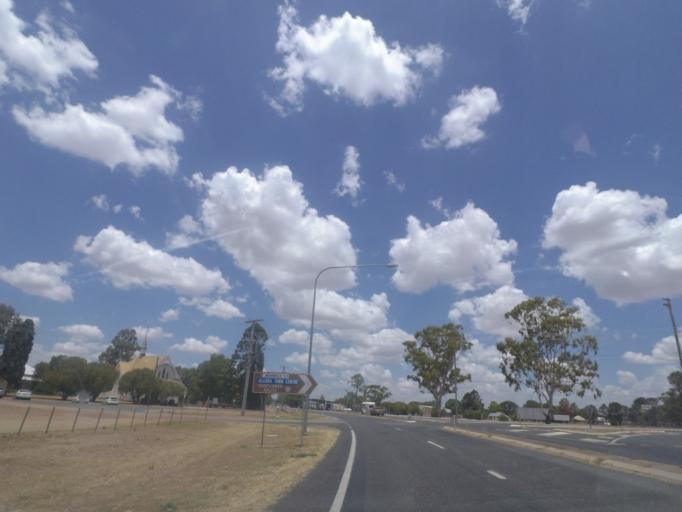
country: AU
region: Queensland
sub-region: Southern Downs
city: Warwick
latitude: -28.0358
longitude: 151.9880
